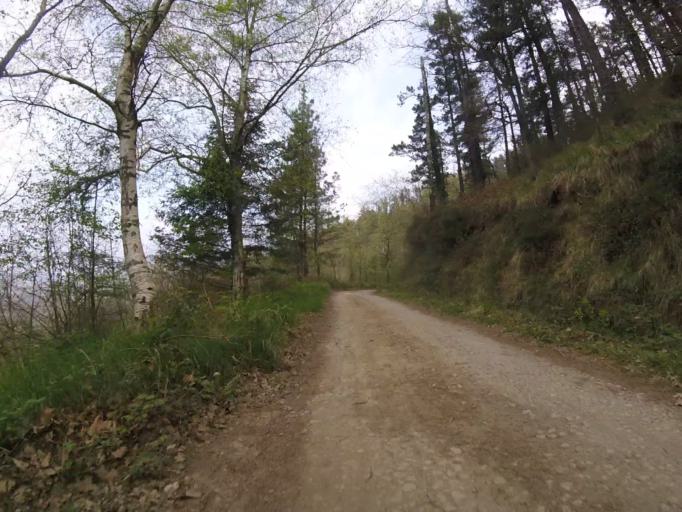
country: ES
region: Basque Country
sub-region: Provincia de Guipuzcoa
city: Usurbil
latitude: 43.2509
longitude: -2.0834
